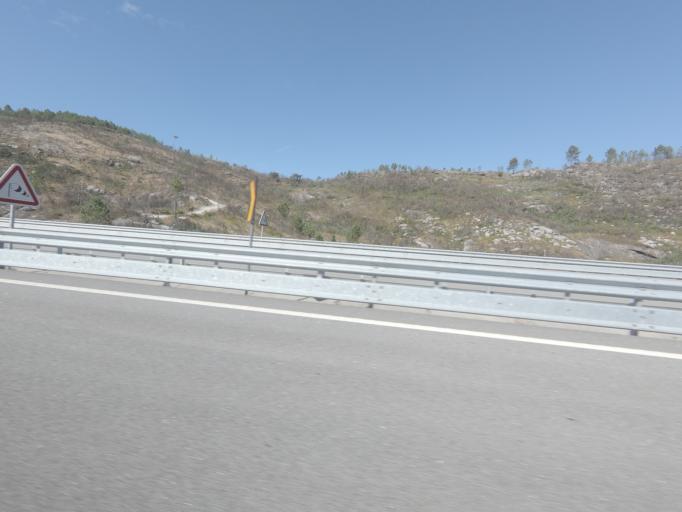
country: PT
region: Porto
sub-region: Amarante
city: Amarante
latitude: 41.2518
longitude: -7.9950
